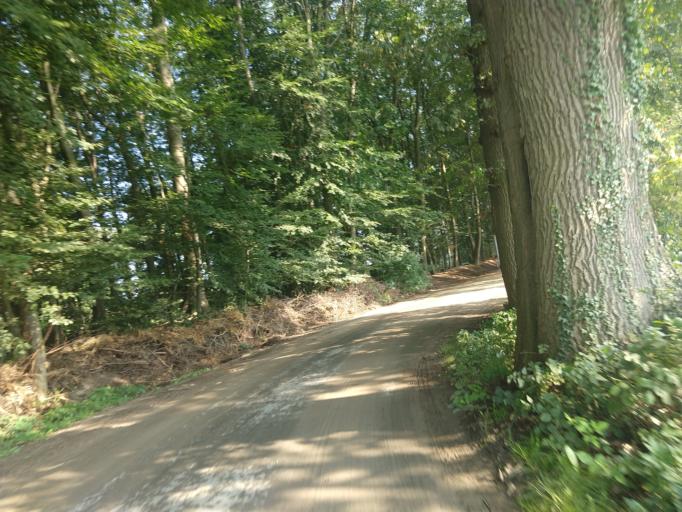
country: NL
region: Gelderland
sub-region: Gemeente Lochem
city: Eefde
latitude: 52.1655
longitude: 6.2467
